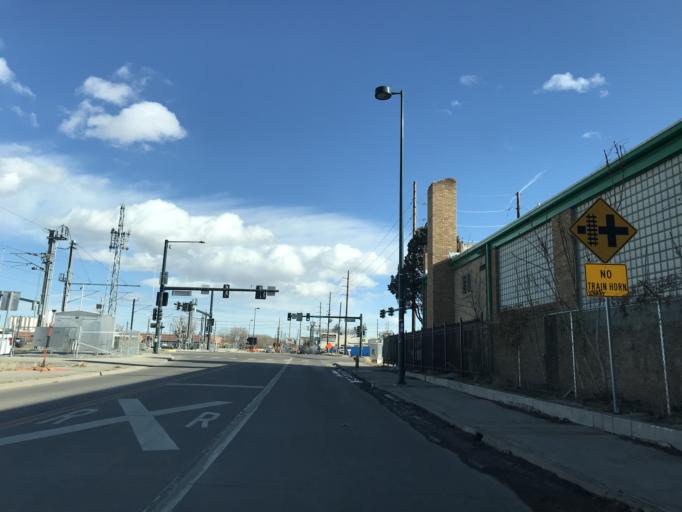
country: US
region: Colorado
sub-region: Denver County
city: Denver
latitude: 39.7728
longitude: -104.9604
